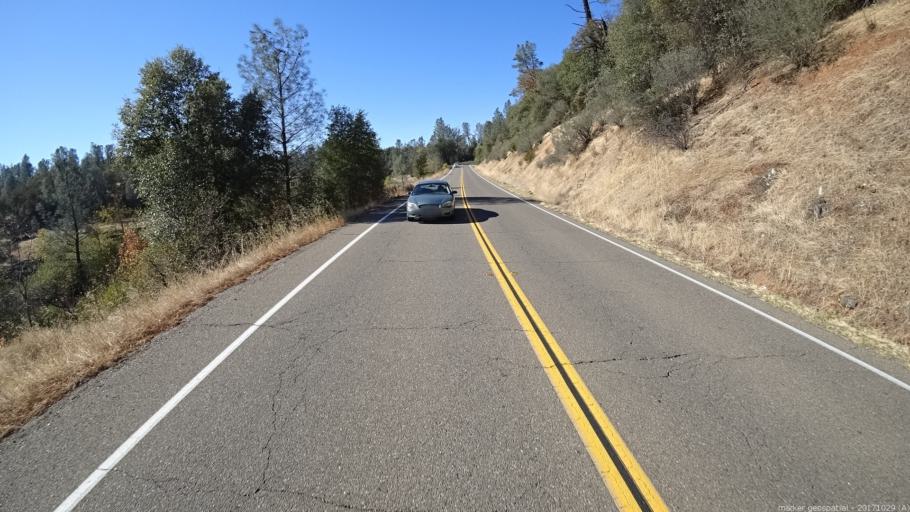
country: US
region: California
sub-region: Shasta County
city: Shasta
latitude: 40.4937
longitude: -122.4694
